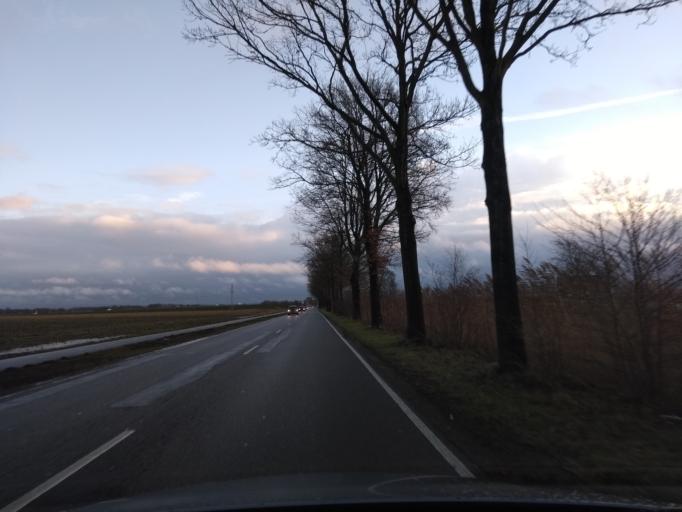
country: NL
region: Overijssel
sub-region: Gemeente Twenterand
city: Vriezenveen
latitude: 52.3932
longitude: 6.6147
